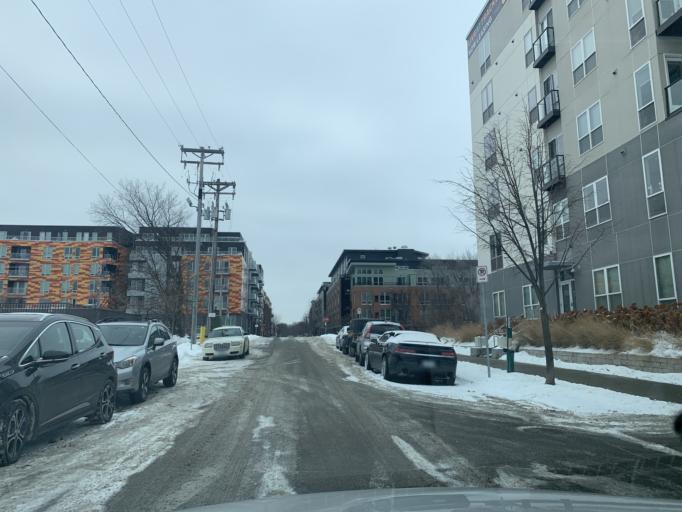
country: US
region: Minnesota
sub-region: Hennepin County
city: Minneapolis
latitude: 44.9509
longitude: -93.2894
